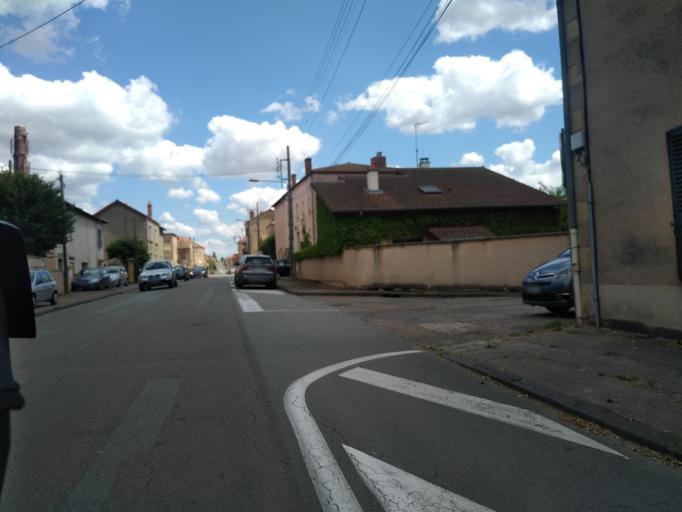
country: FR
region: Rhone-Alpes
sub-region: Departement de la Loire
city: Pouilly-sous-Charlieu
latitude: 46.1466
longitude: 4.1036
